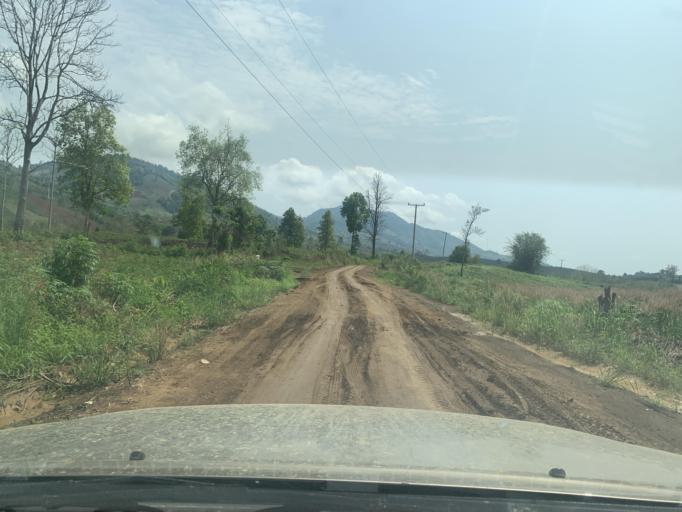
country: TH
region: Uttaradit
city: Ban Khok
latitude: 18.3535
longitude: 101.3785
